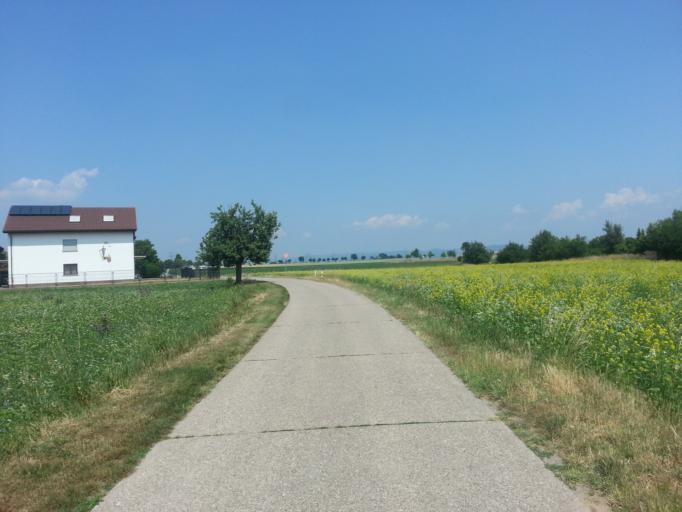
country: DE
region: Baden-Wuerttemberg
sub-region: Karlsruhe Region
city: Ilvesheim
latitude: 49.4818
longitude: 8.5680
